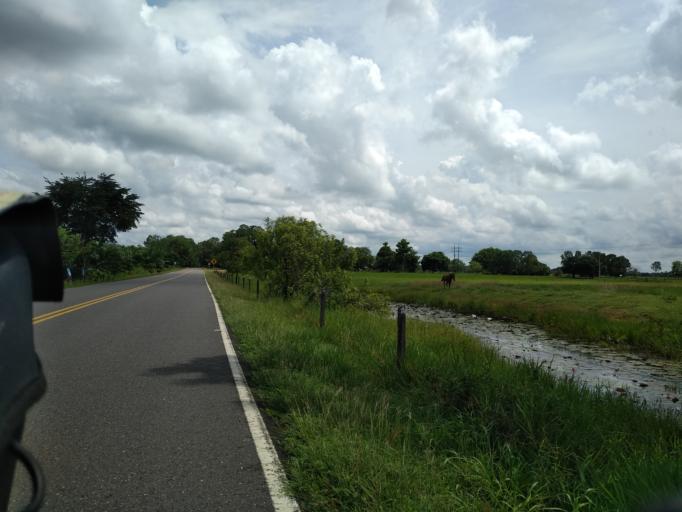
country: CO
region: Santander
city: Puerto Parra
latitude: 6.4974
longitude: -74.0523
